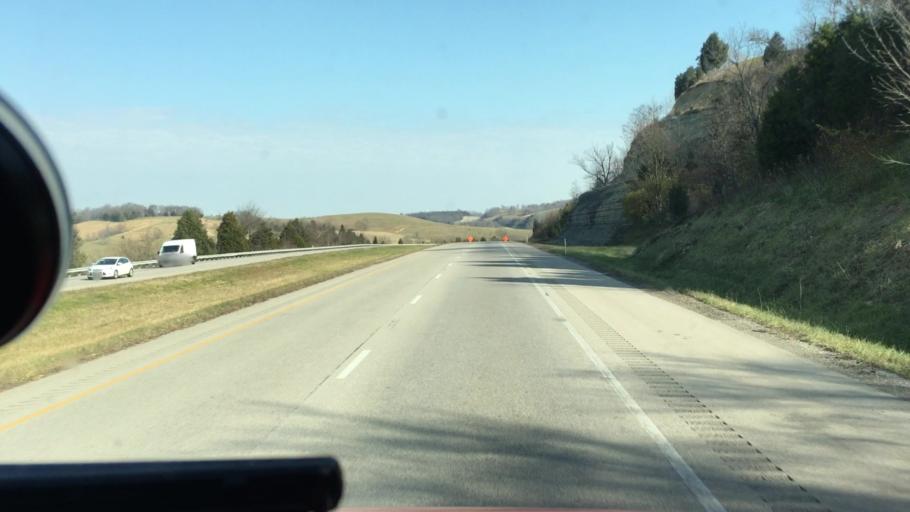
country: US
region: Kentucky
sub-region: Bath County
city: Owingsville
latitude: 38.1082
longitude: -83.8191
